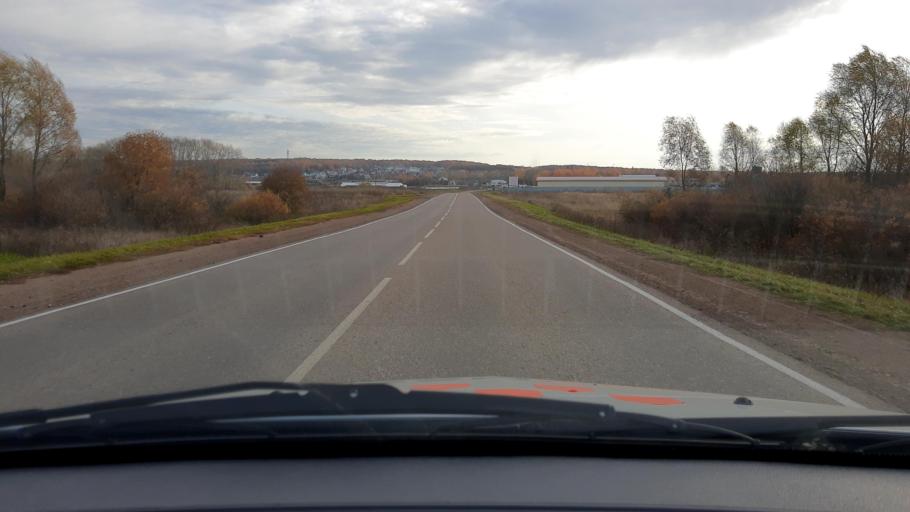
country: RU
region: Bashkortostan
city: Avdon
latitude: 54.8218
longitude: 55.6776
